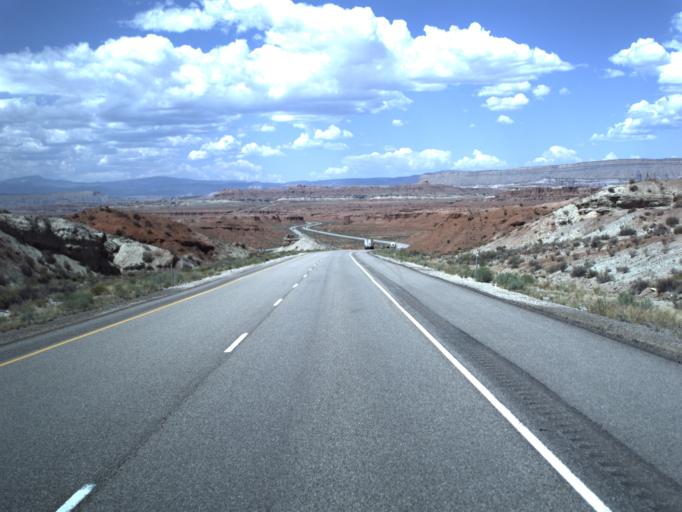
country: US
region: Utah
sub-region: Emery County
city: Ferron
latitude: 38.8476
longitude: -111.0204
